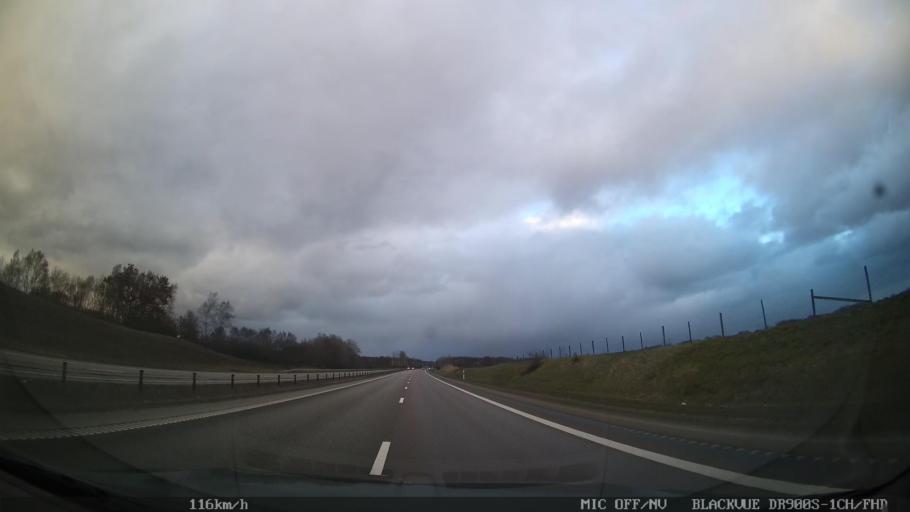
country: SE
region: Skane
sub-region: Astorps Kommun
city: Kvidinge
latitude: 56.1999
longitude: 13.0762
